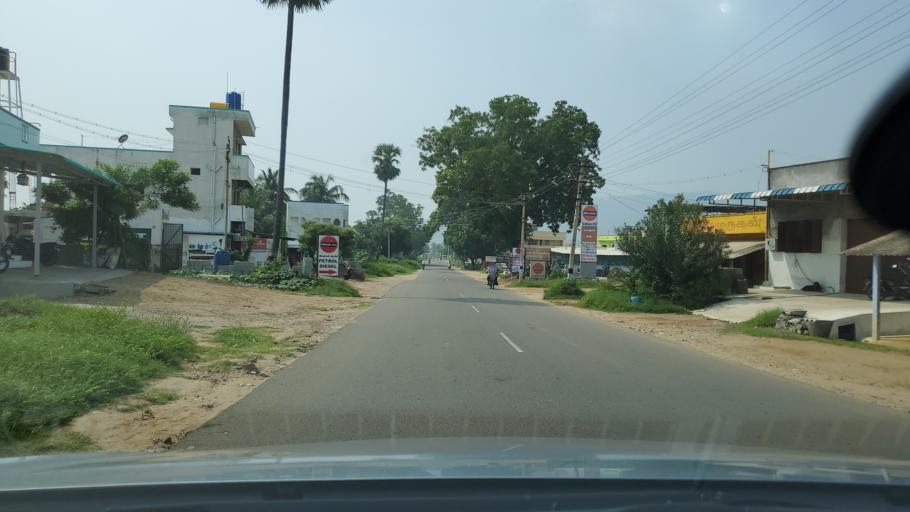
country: IN
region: Tamil Nadu
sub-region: Erode
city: Chennimalai
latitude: 11.1772
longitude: 77.6065
